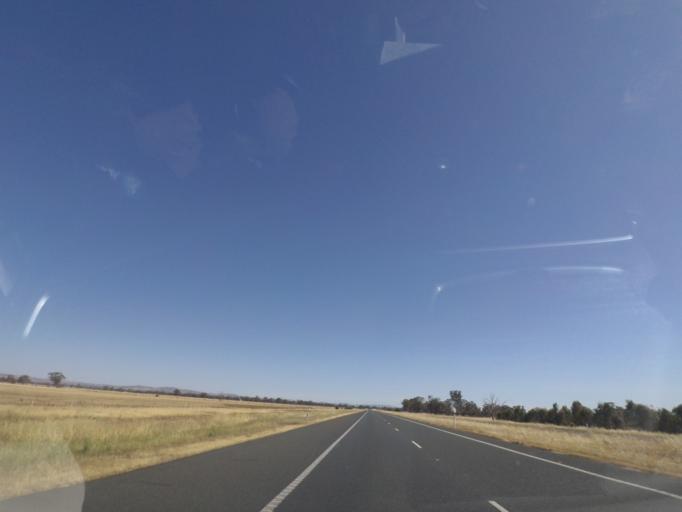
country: AU
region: Victoria
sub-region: Greater Shepparton
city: Shepparton
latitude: -36.7850
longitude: 145.1785
